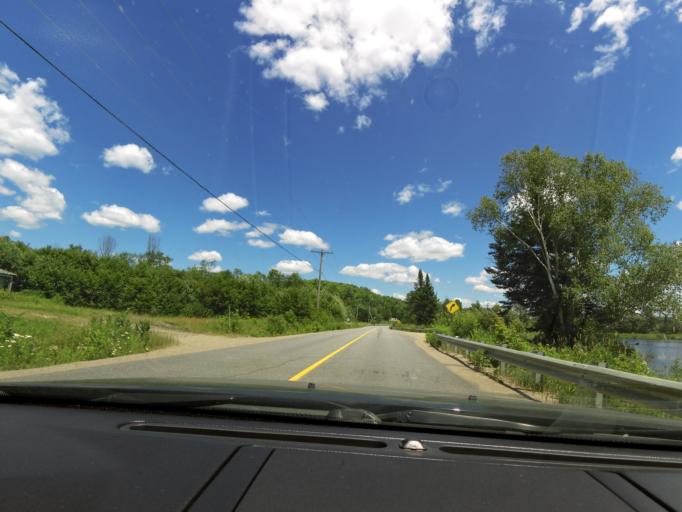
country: CA
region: Ontario
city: Huntsville
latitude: 45.5864
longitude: -79.2171
